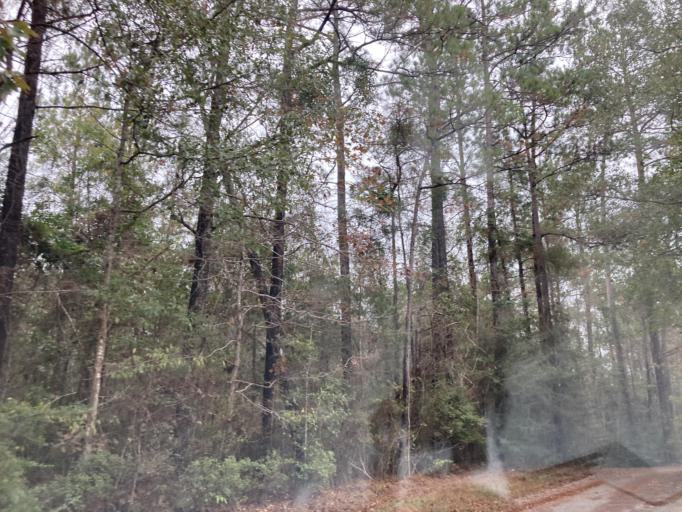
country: US
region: Mississippi
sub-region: Lamar County
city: Purvis
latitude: 31.1940
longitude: -89.4469
